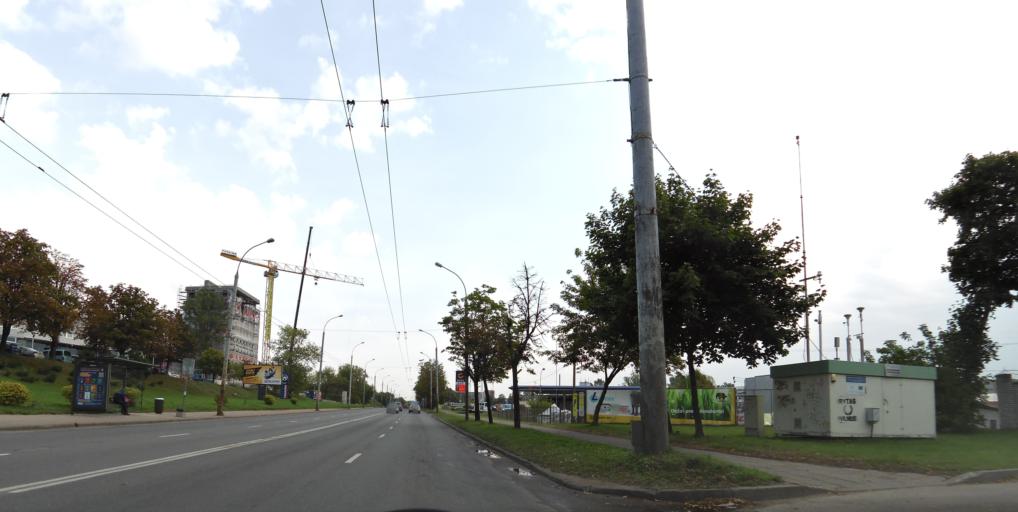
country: LT
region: Vilnius County
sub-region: Vilnius
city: Vilnius
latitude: 54.7153
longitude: 25.2890
